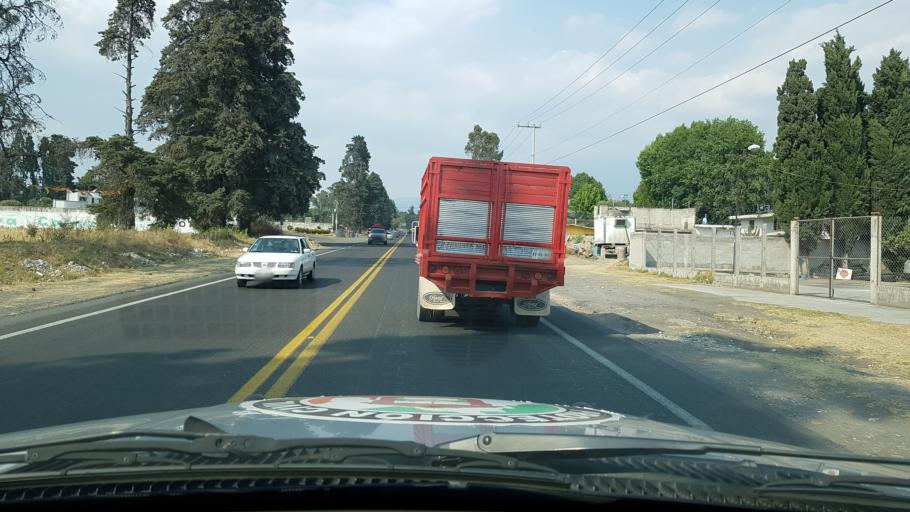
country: MX
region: Mexico
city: Ozumba de Alzate
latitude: 19.0497
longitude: -98.7918
